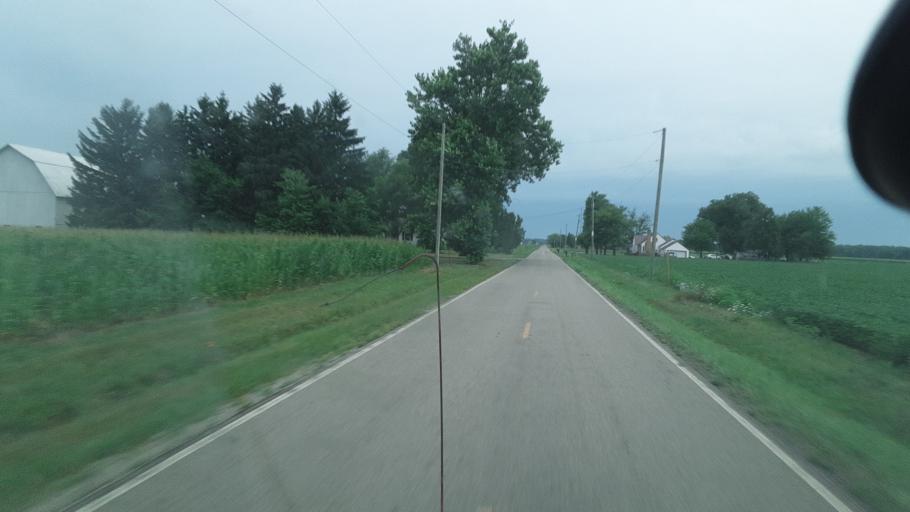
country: US
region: Ohio
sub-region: Defiance County
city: Hicksville
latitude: 41.2670
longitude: -84.7442
